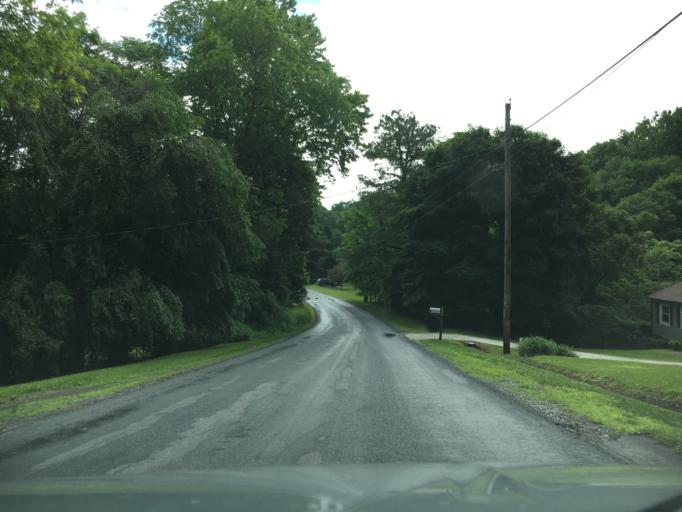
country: US
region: Virginia
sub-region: Bedford County
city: Forest
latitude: 37.3596
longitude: -79.2619
